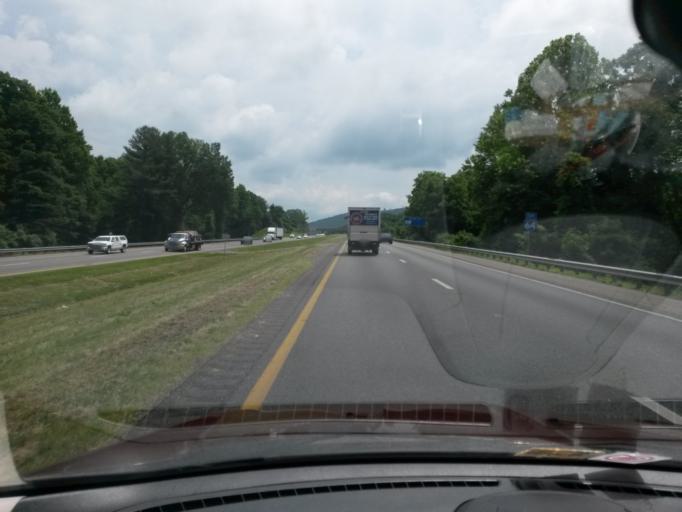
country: US
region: Virginia
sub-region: City of Charlottesville
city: Charlottesville
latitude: 38.0073
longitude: -78.5001
